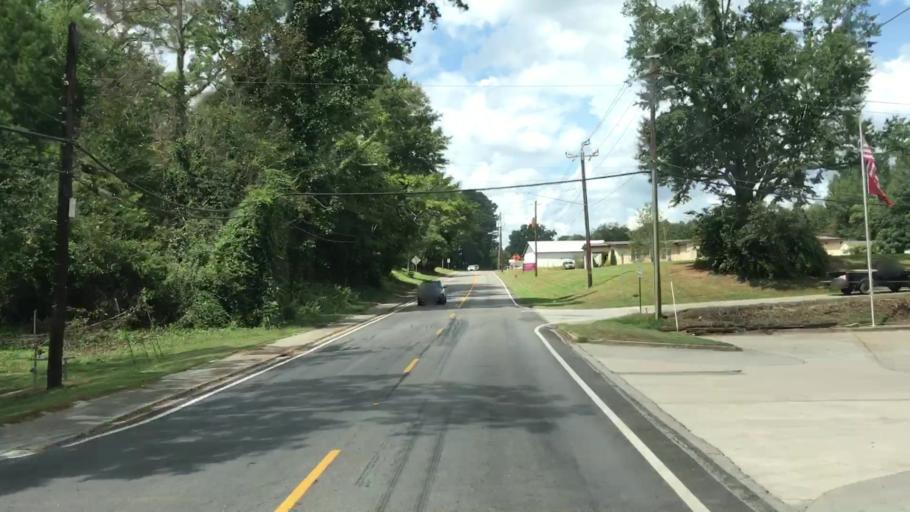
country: US
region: Georgia
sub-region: Greene County
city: Greensboro
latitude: 33.5739
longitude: -83.1751
